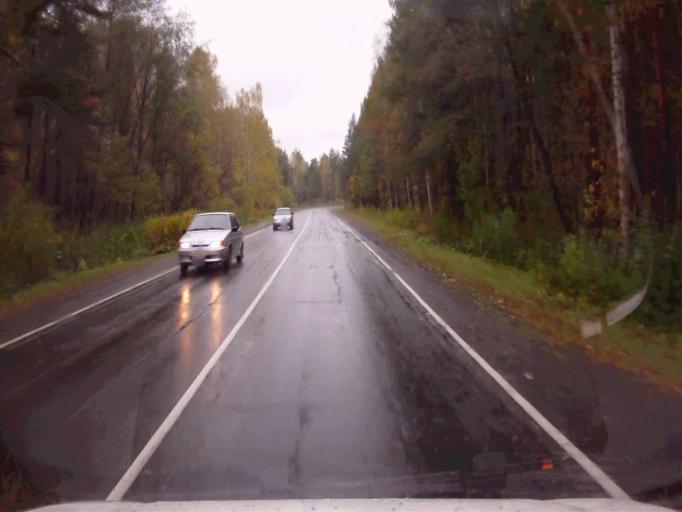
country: RU
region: Chelyabinsk
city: Verkhniy Ufaley
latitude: 55.9589
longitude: 60.3869
